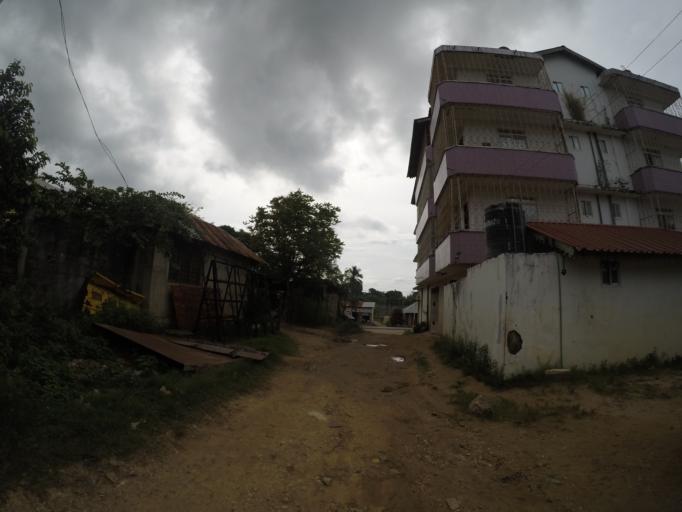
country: TZ
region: Pemba South
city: Chake Chake
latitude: -5.2518
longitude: 39.7754
